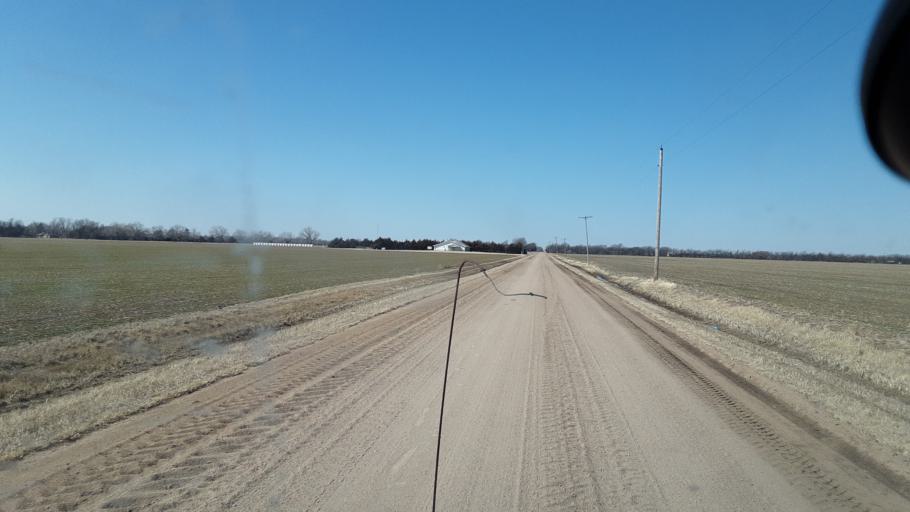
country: US
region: Kansas
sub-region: Reno County
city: South Hutchinson
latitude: 37.9846
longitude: -98.0178
